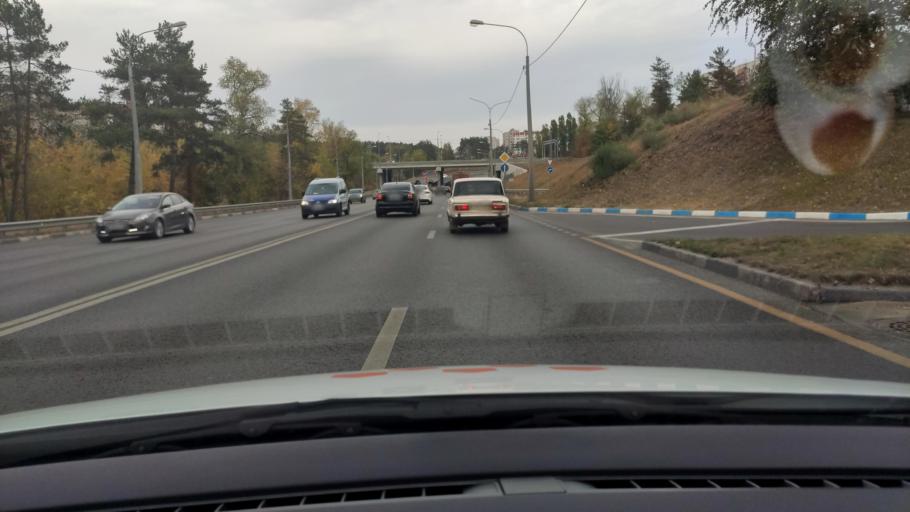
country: RU
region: Voronezj
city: Pridonskoy
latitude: 51.6819
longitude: 39.1172
